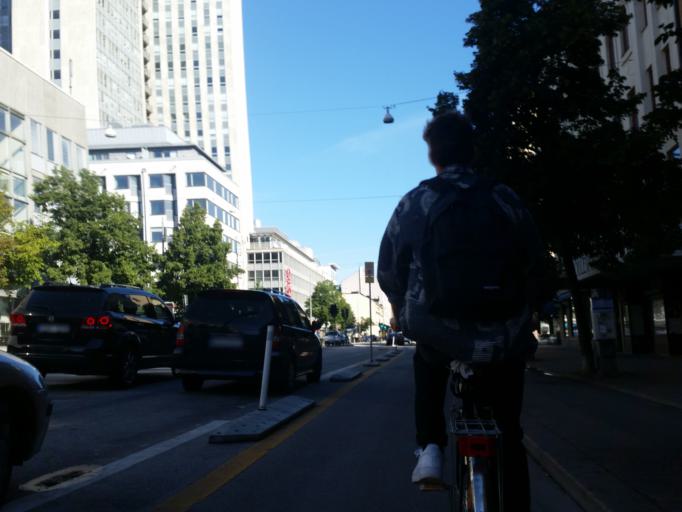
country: SE
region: Stockholm
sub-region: Stockholms Kommun
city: Stockholm
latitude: 59.3110
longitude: 18.0750
